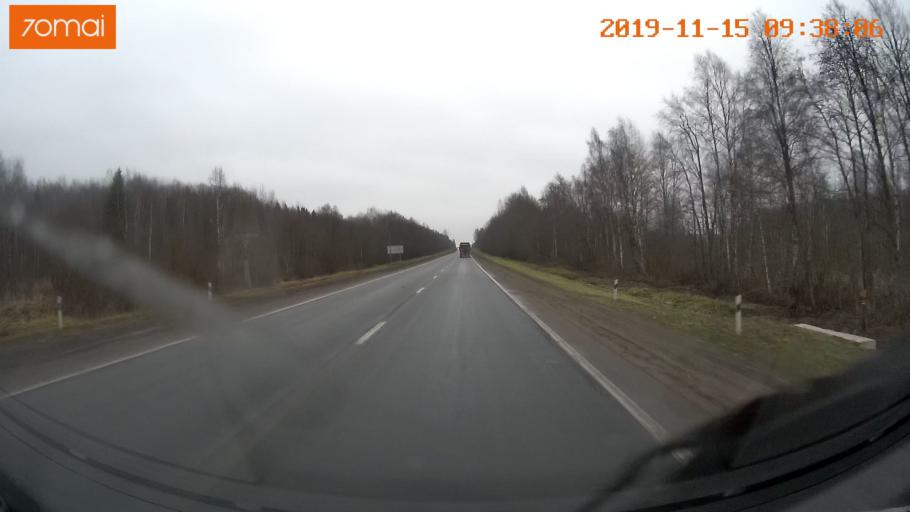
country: RU
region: Vologda
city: Sheksna
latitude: 59.2350
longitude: 38.4490
